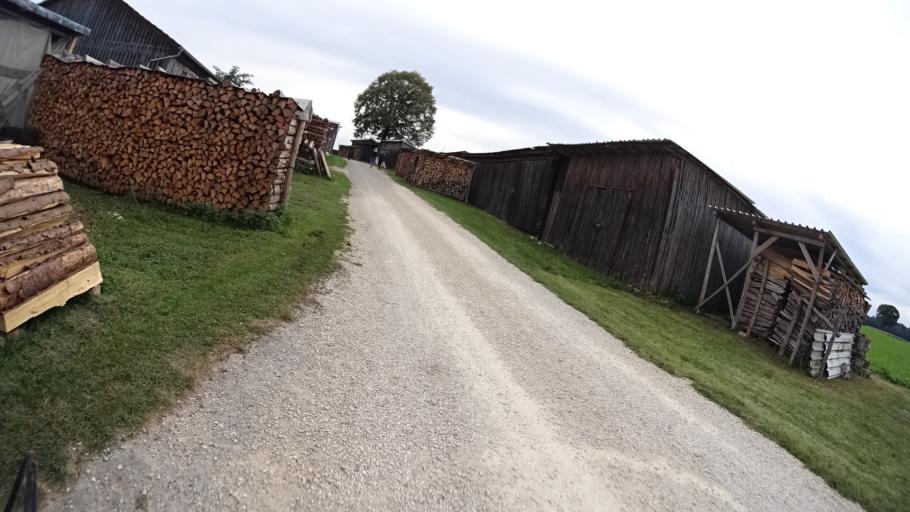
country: DE
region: Bavaria
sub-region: Upper Bavaria
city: Hitzhofen
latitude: 48.8796
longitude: 11.3316
